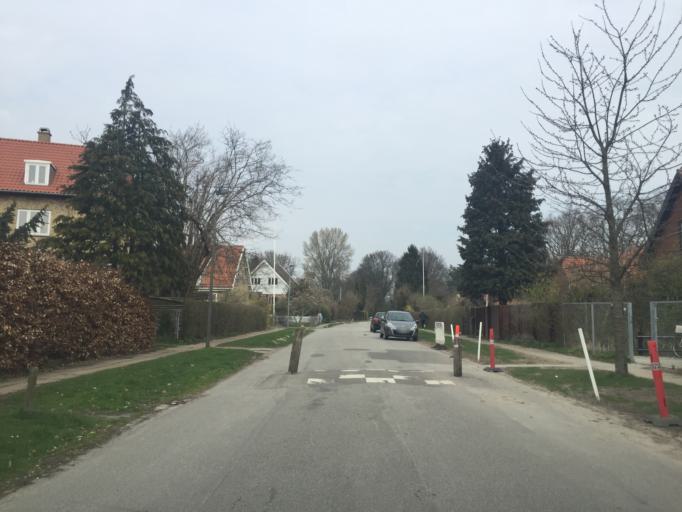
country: DK
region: Capital Region
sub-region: Kobenhavn
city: Vanlose
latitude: 55.7099
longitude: 12.4989
